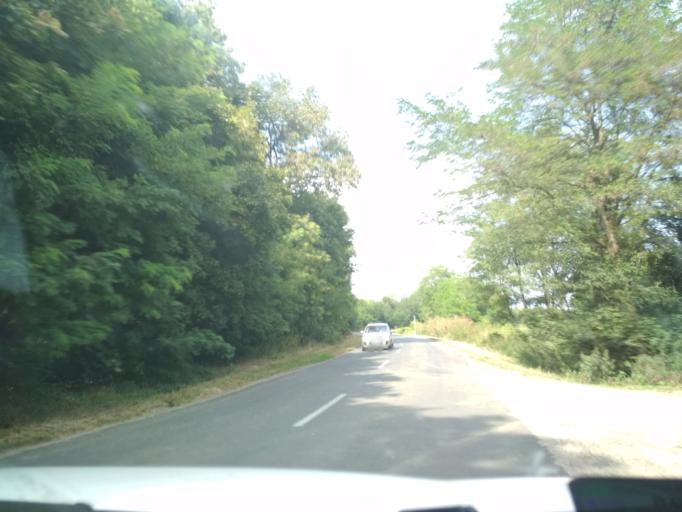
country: HU
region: Jasz-Nagykun-Szolnok
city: Tiszaszolos
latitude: 47.5229
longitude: 20.6686
